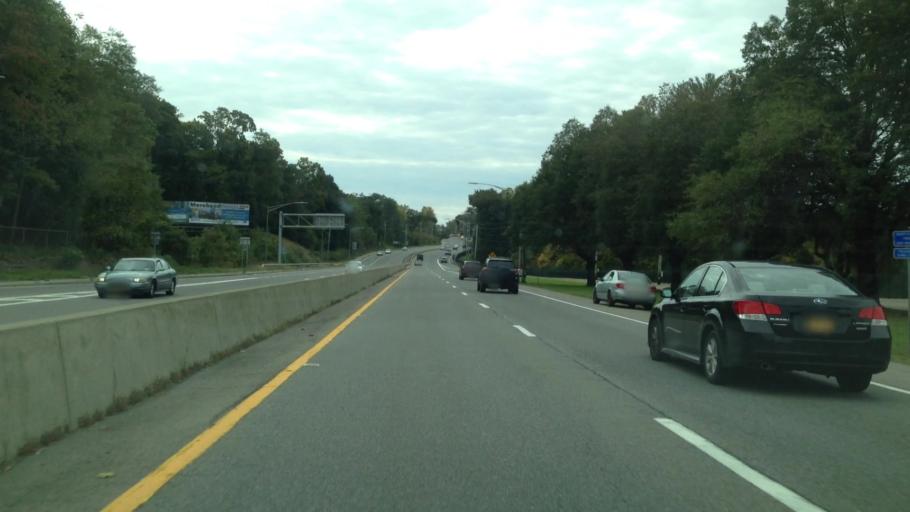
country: US
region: New York
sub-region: Dutchess County
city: Poughkeepsie
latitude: 41.6854
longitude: -73.9304
